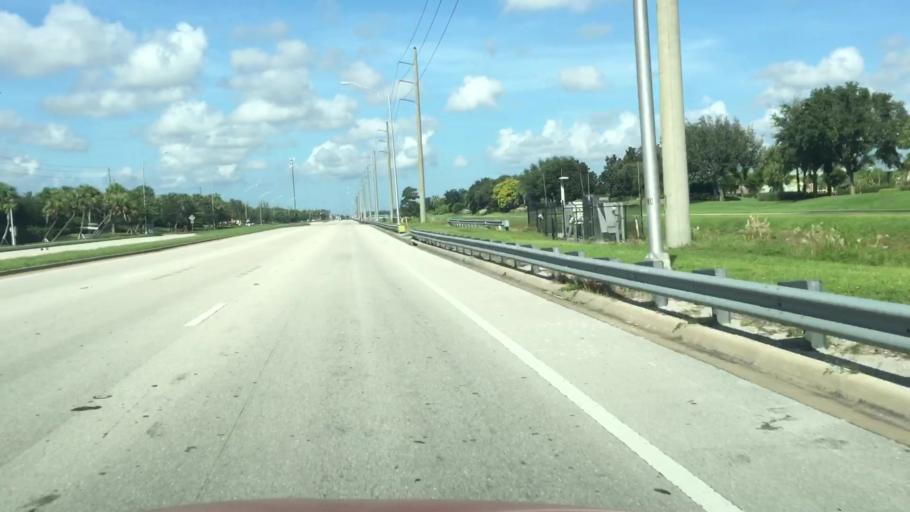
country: US
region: Florida
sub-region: Collier County
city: Vineyards
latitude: 26.2732
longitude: -81.6736
